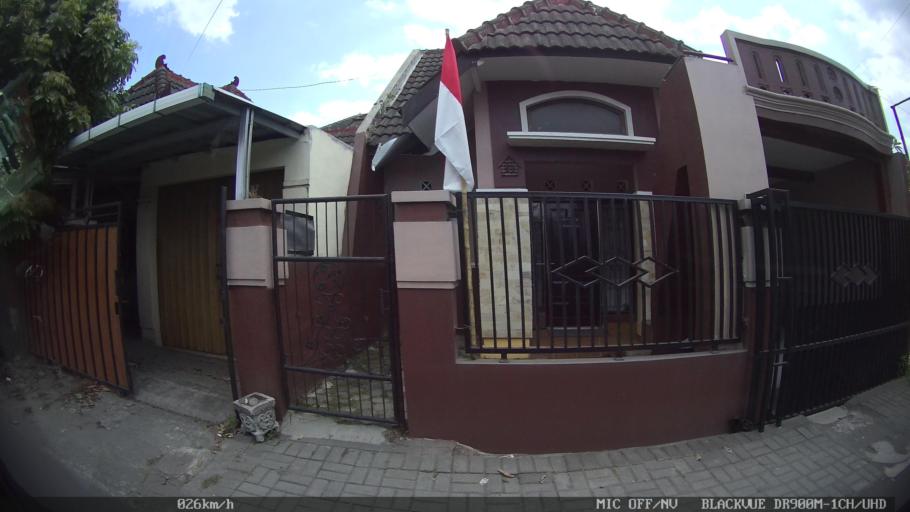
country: ID
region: Daerah Istimewa Yogyakarta
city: Kasihan
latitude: -7.8102
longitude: 110.3442
